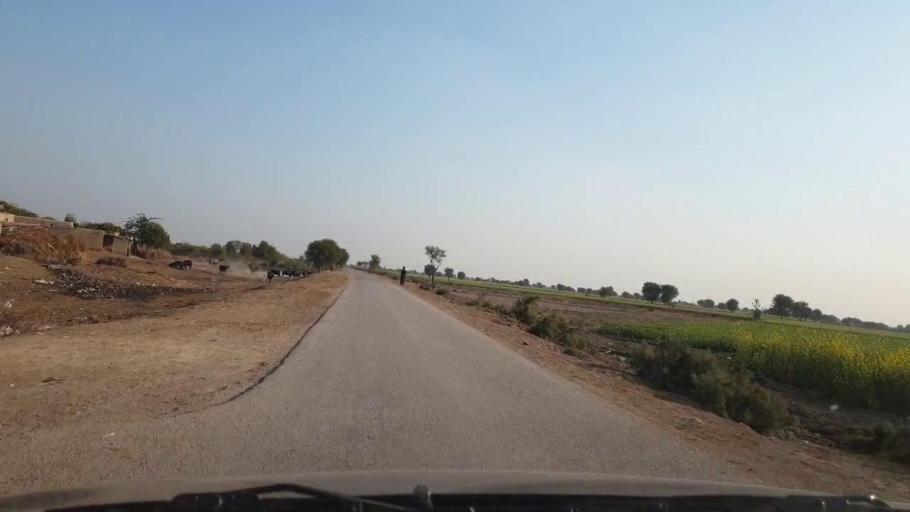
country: PK
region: Sindh
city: Jhol
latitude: 25.9414
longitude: 68.9094
